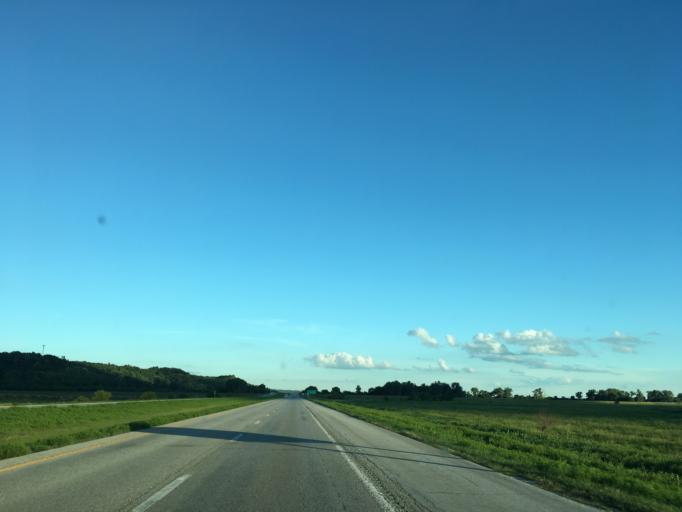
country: US
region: Iowa
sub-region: Fremont County
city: Hamburg
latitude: 40.5801
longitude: -95.6490
